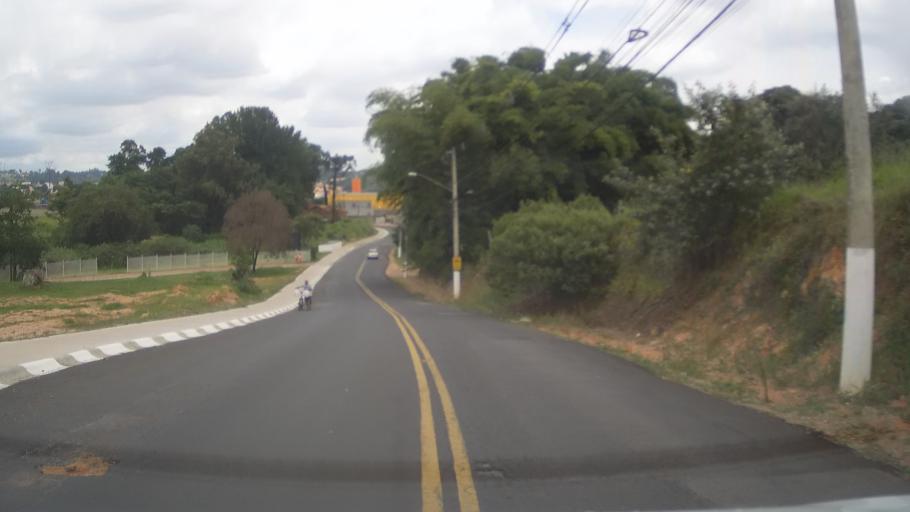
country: BR
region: Sao Paulo
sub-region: Itupeva
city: Itupeva
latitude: -23.1528
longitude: -47.0460
